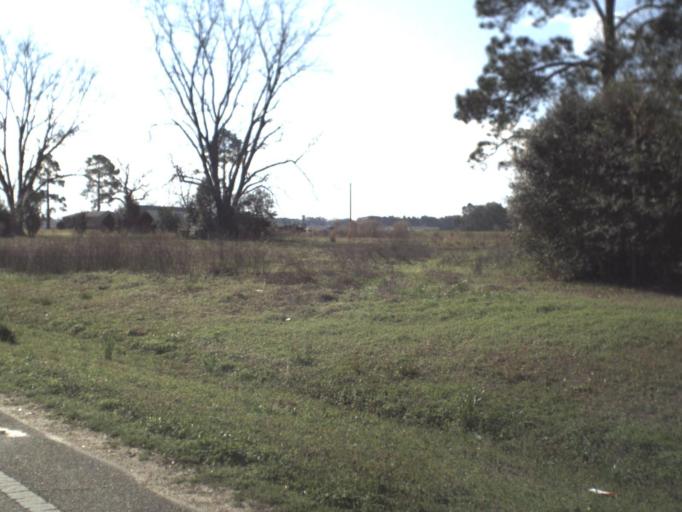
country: US
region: Florida
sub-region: Jackson County
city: Malone
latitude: 30.9780
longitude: -85.1736
